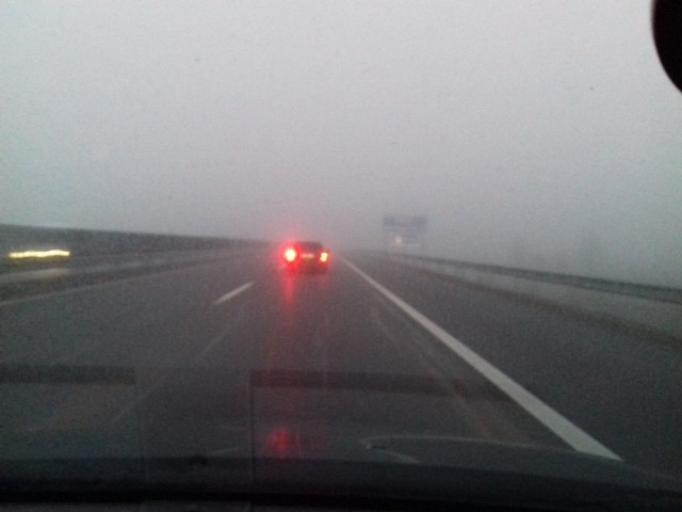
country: HU
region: Hajdu-Bihar
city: Hajdunanas
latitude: 47.8834
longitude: 21.4214
